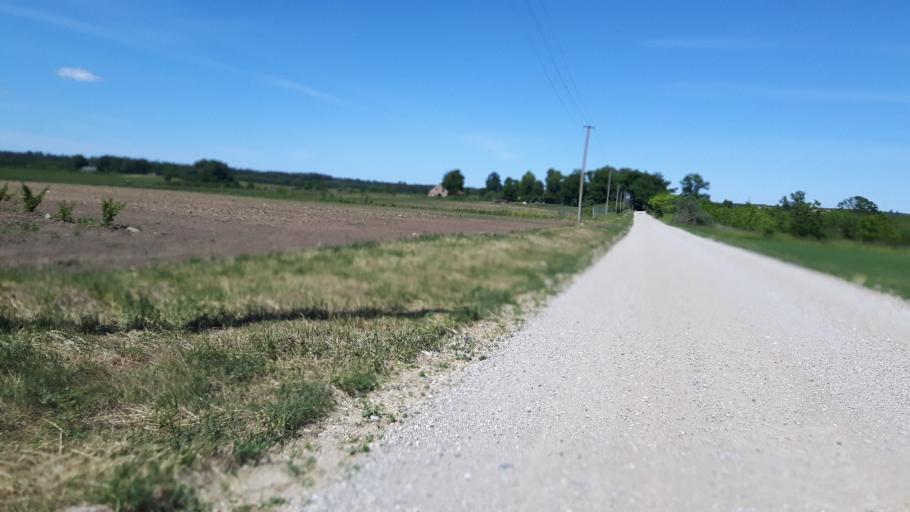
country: LV
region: Kandava
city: Kandava
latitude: 57.0405
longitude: 22.8810
